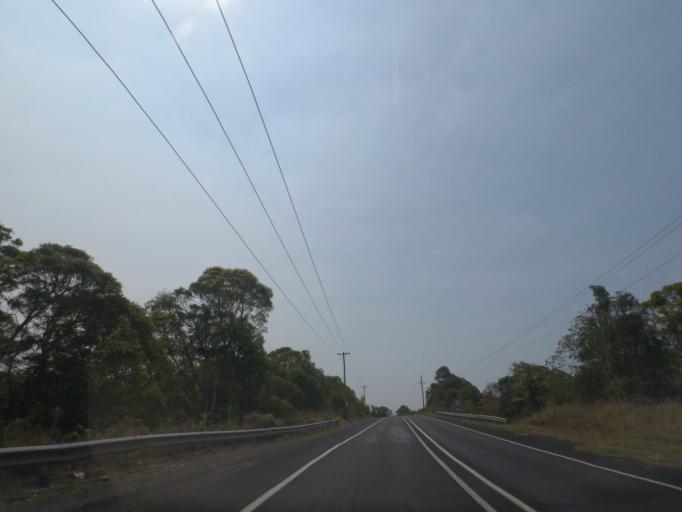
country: AU
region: New South Wales
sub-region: Byron Shire
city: Brunswick Heads
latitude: -28.5230
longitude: 153.5305
